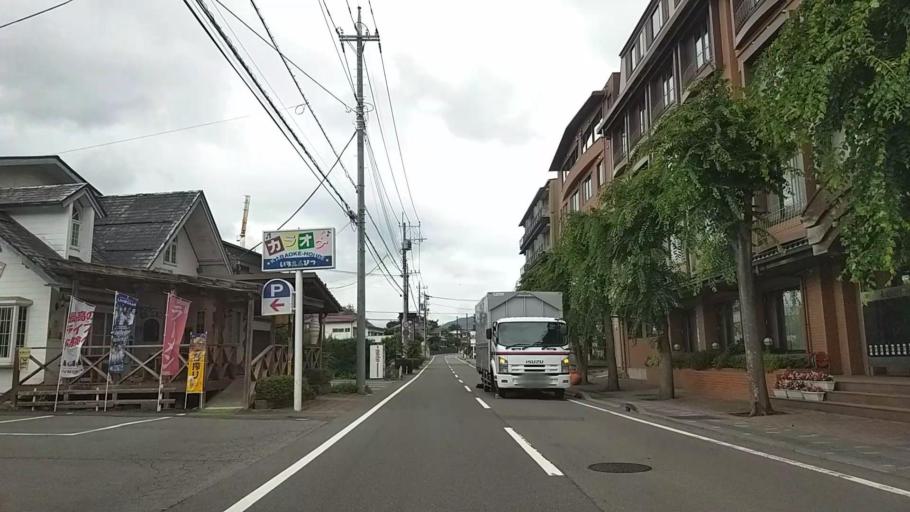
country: JP
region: Yamanashi
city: Fujikawaguchiko
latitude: 35.5053
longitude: 138.7619
